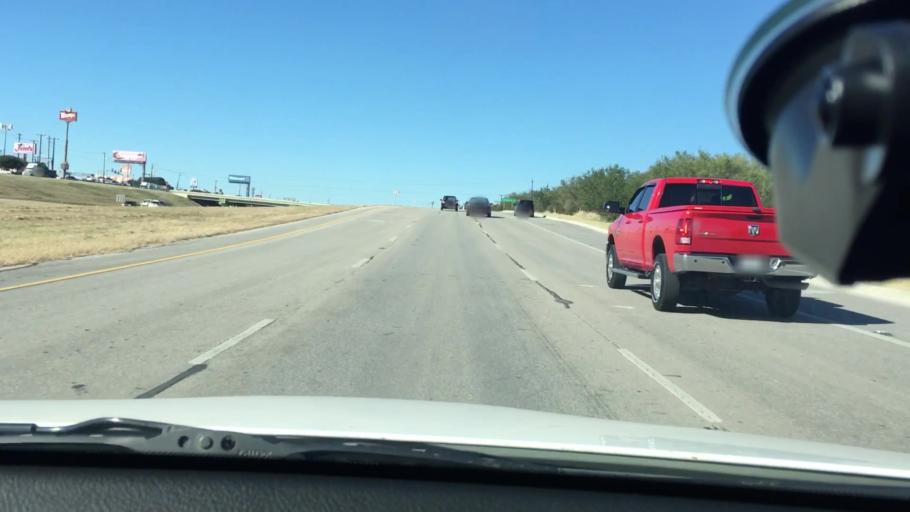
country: US
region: Texas
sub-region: Bexar County
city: Live Oak
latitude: 29.5895
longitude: -98.3497
